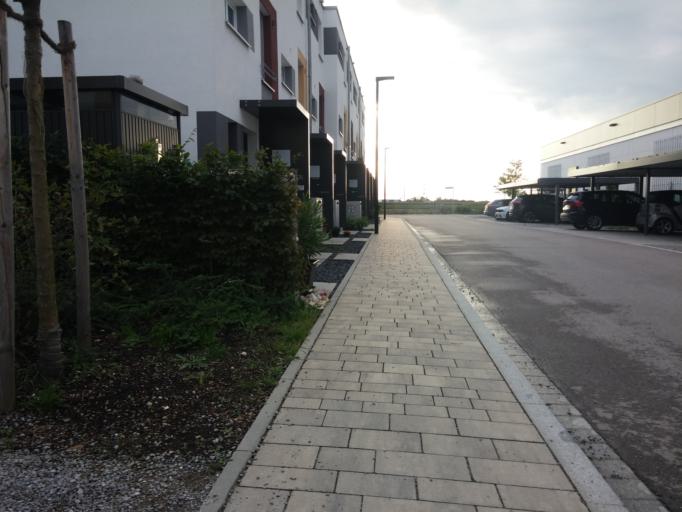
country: DE
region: Bavaria
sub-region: Upper Bavaria
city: Pliening
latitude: 48.1804
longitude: 11.7964
